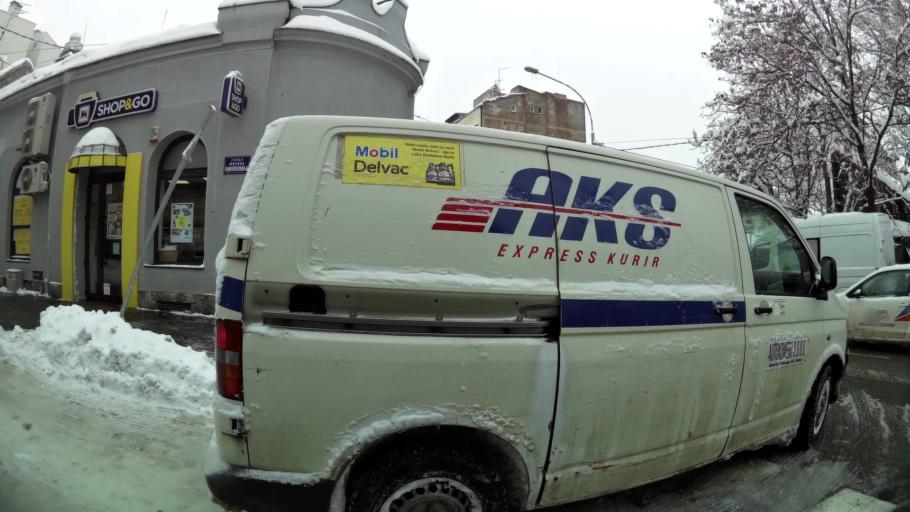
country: RS
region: Central Serbia
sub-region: Belgrade
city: Vracar
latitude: 44.7968
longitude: 20.4773
